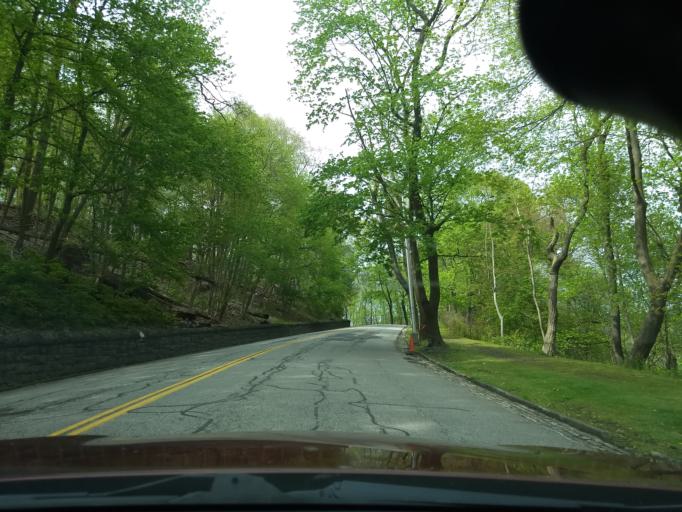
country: US
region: Pennsylvania
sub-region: Allegheny County
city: Aspinwall
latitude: 40.4836
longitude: -79.9123
